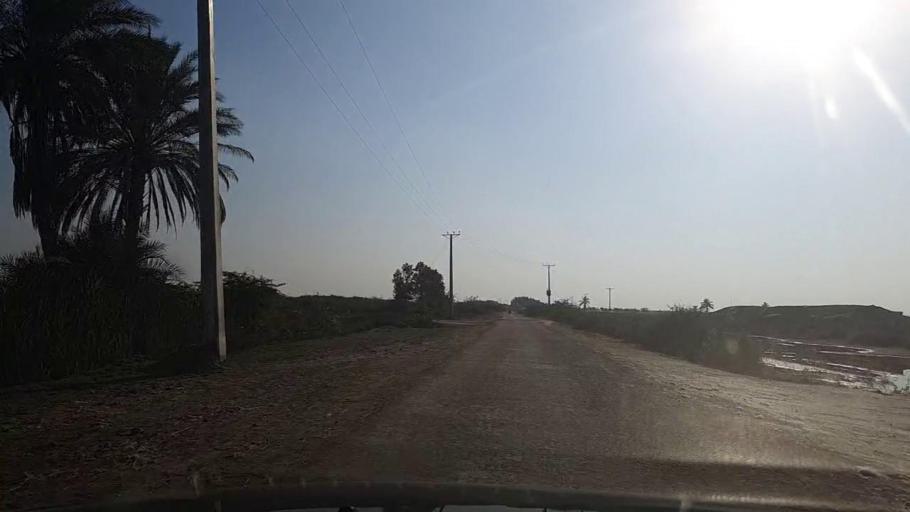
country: PK
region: Sindh
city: Gharo
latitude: 24.7169
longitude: 67.6880
